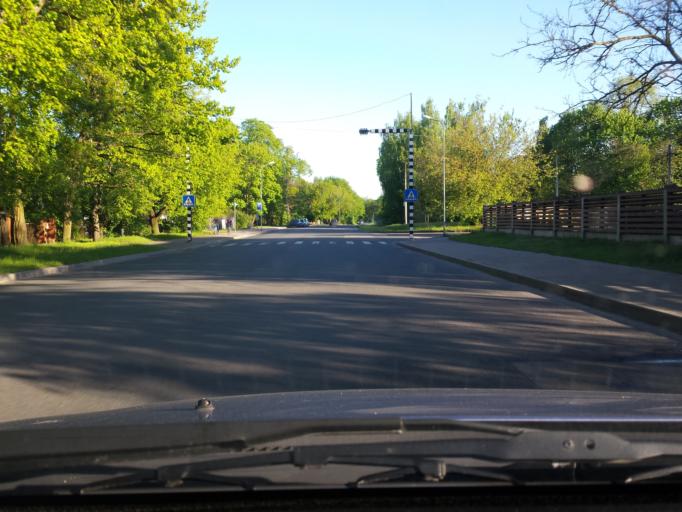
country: LV
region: Riga
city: Jaunciems
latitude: 56.9988
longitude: 24.1705
